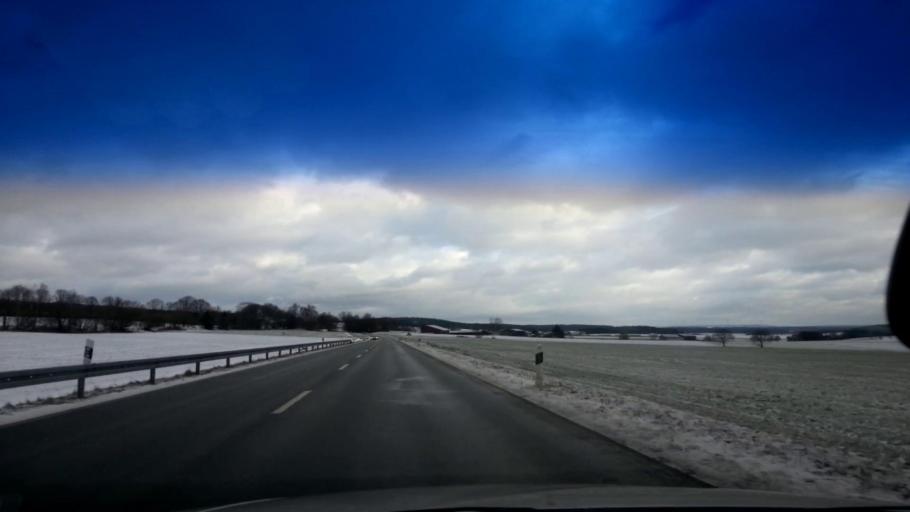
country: DE
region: Bavaria
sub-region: Upper Franconia
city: Grub
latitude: 50.1239
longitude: 11.9124
